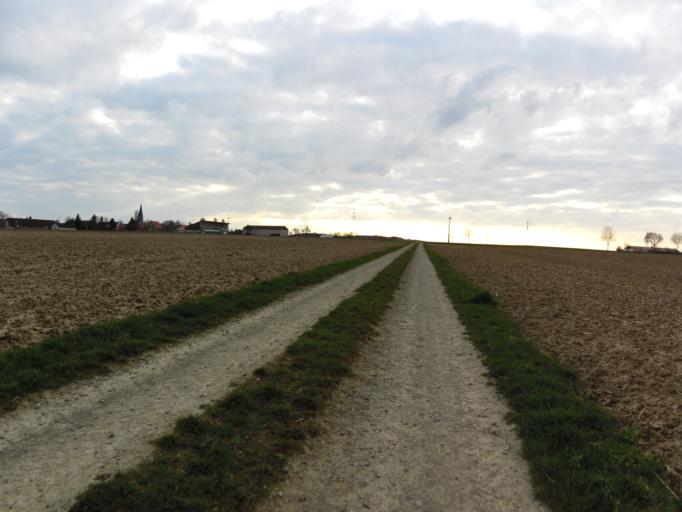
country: DE
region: Bavaria
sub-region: Regierungsbezirk Unterfranken
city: Biebelried
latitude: 49.7484
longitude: 10.0707
